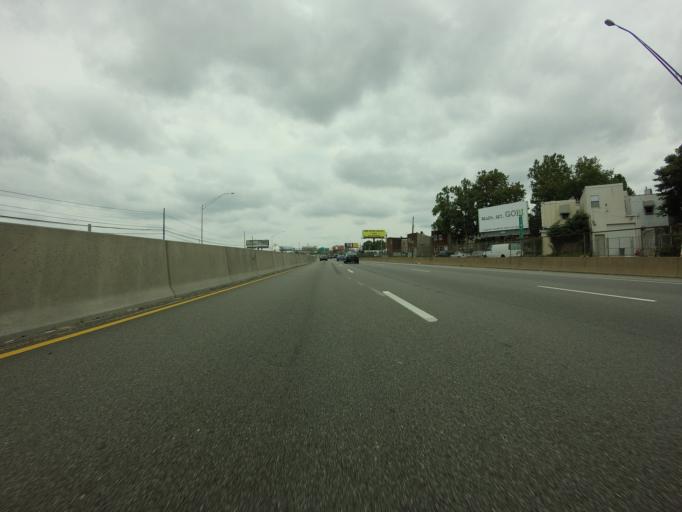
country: US
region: Pennsylvania
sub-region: Philadelphia County
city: Philadelphia
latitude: 39.9257
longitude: -75.1939
